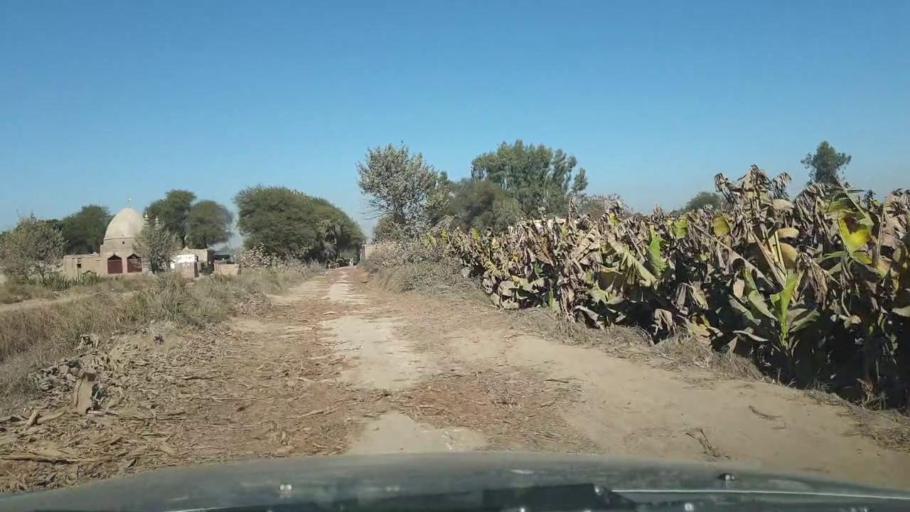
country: PK
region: Sindh
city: Ghotki
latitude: 28.0423
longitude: 69.2468
